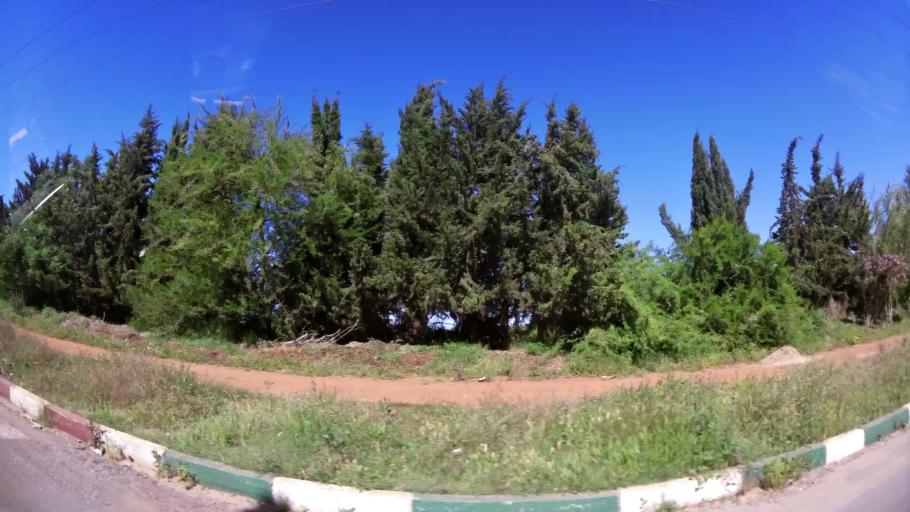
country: MA
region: Oriental
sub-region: Berkane-Taourirt
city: Berkane
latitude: 34.9444
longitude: -2.3262
